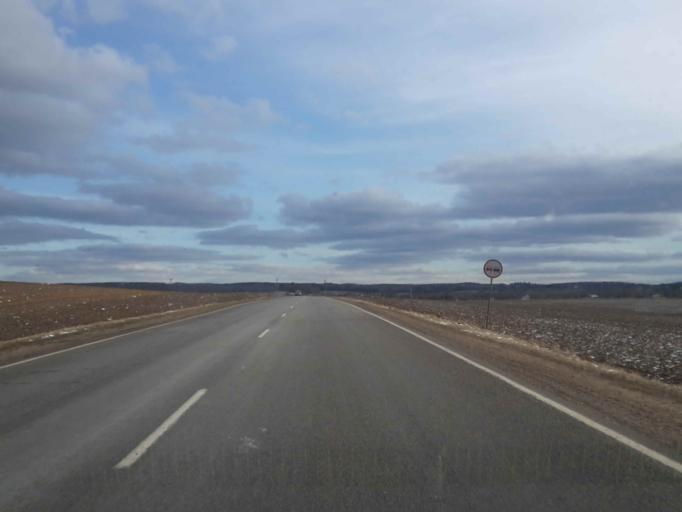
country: BY
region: Minsk
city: Il'ya
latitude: 54.3050
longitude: 27.4745
